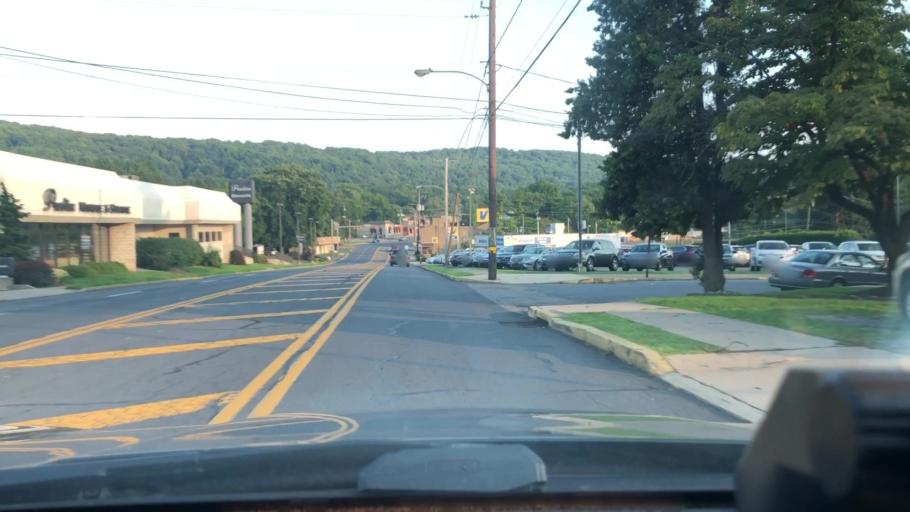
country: US
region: Pennsylvania
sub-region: Lehigh County
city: Emmaus
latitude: 40.5452
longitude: -75.4880
